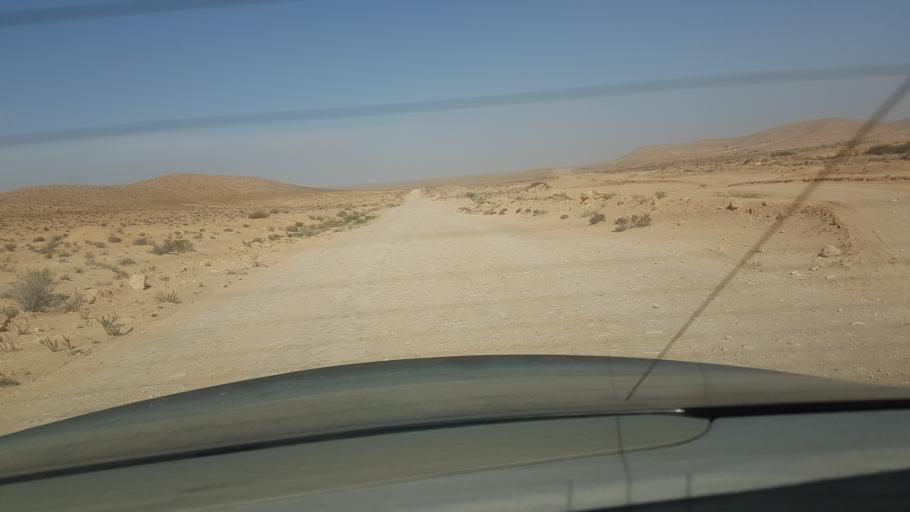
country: TN
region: Qabis
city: Matmata
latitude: 33.6410
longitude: 9.7370
